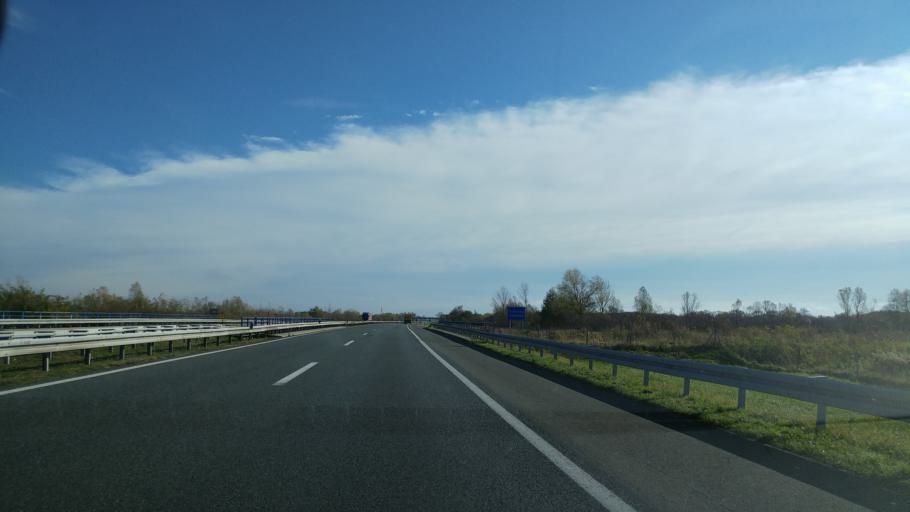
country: HR
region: Brodsko-Posavska
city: Okucani
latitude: 45.2558
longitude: 17.1718
